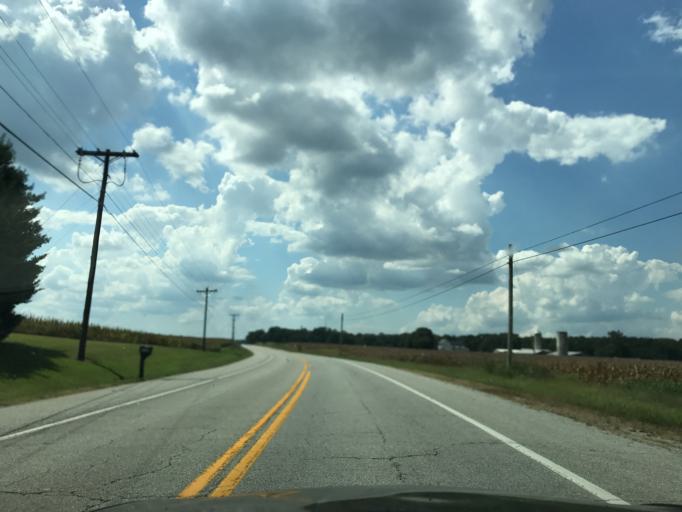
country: US
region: Maryland
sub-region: Queen Anne's County
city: Kingstown
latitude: 39.1838
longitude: -75.8972
